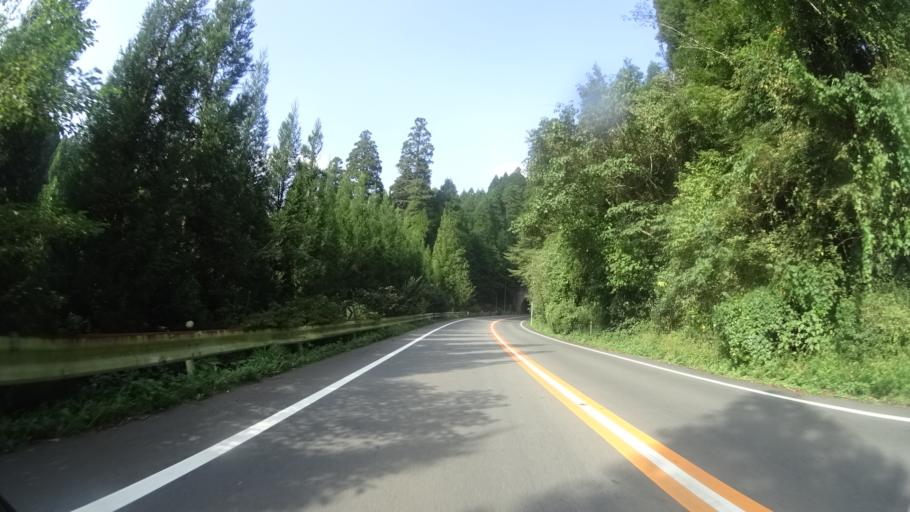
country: JP
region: Kumamoto
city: Aso
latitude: 33.0786
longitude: 131.0611
